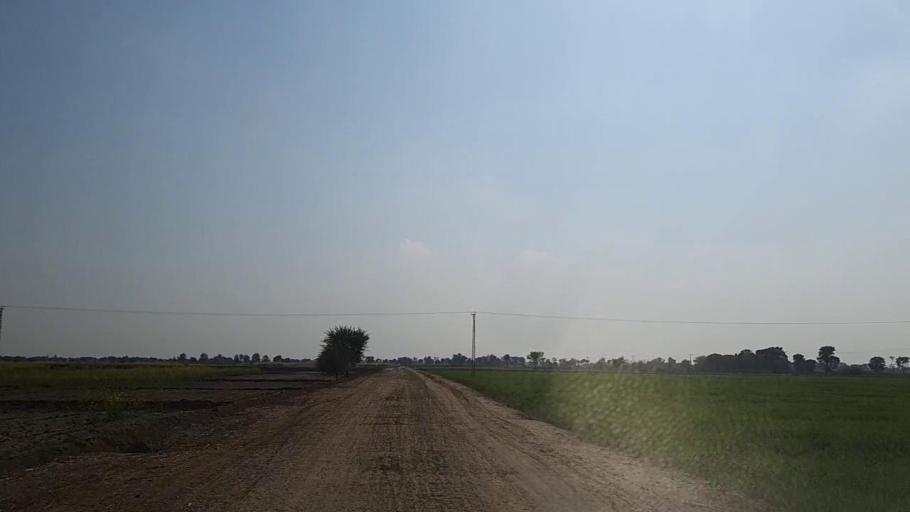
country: PK
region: Sindh
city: Daur
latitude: 26.4438
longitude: 68.2333
